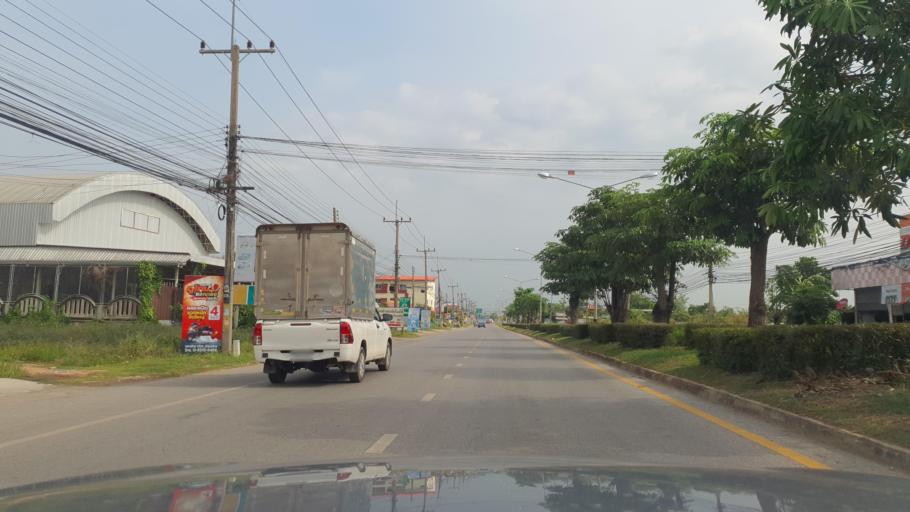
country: TH
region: Phitsanulok
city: Phitsanulok
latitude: 16.8602
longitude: 100.2515
